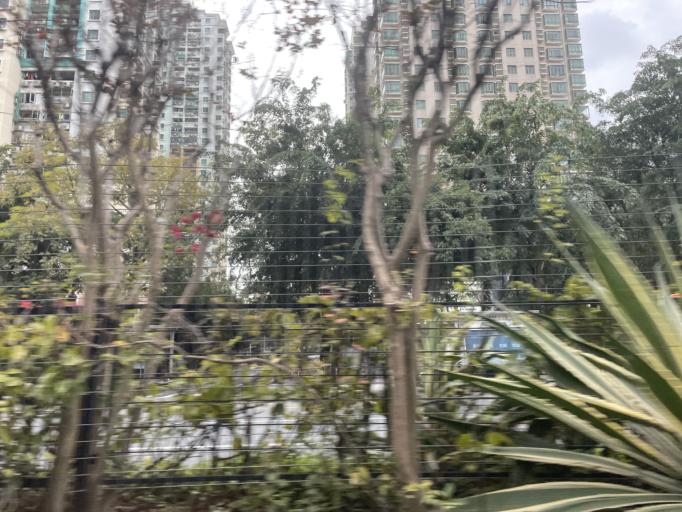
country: CN
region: Guangdong
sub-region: Shenzhen
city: Shenzhen
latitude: 22.5204
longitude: 114.0434
